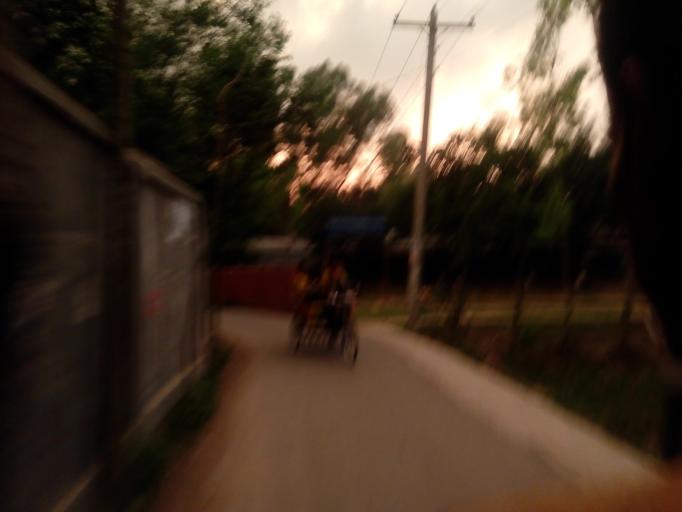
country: BD
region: Rajshahi
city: Sirajganj
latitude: 24.3027
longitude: 89.6925
